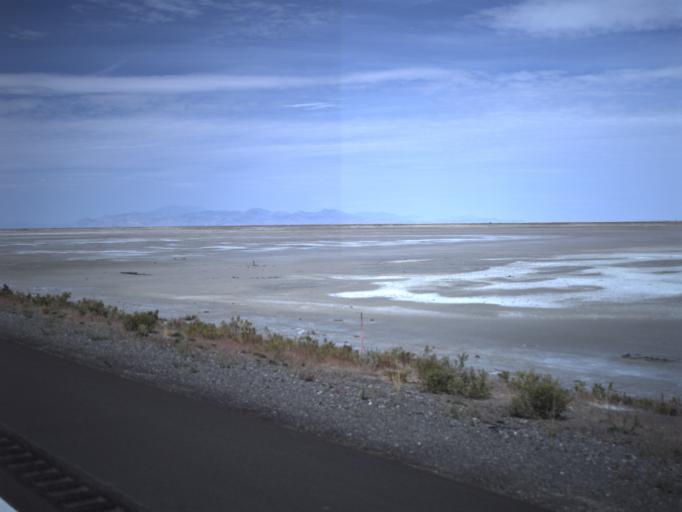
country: US
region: Utah
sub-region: Tooele County
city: Wendover
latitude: 40.7284
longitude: -113.3259
